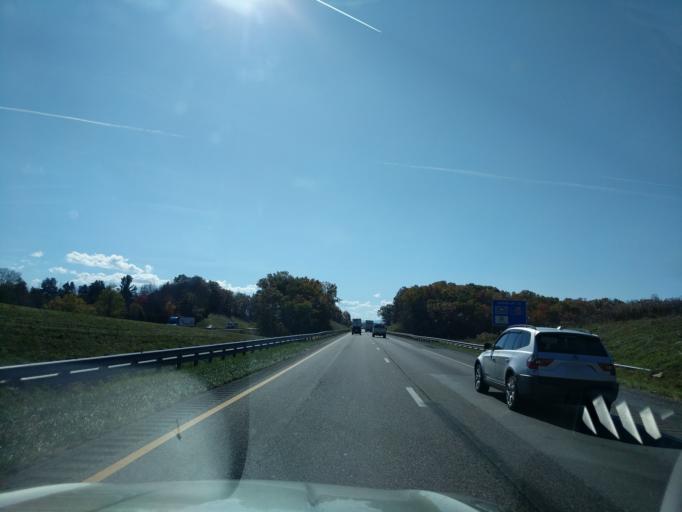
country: US
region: Virginia
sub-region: Augusta County
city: Verona
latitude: 38.1848
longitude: -78.9990
